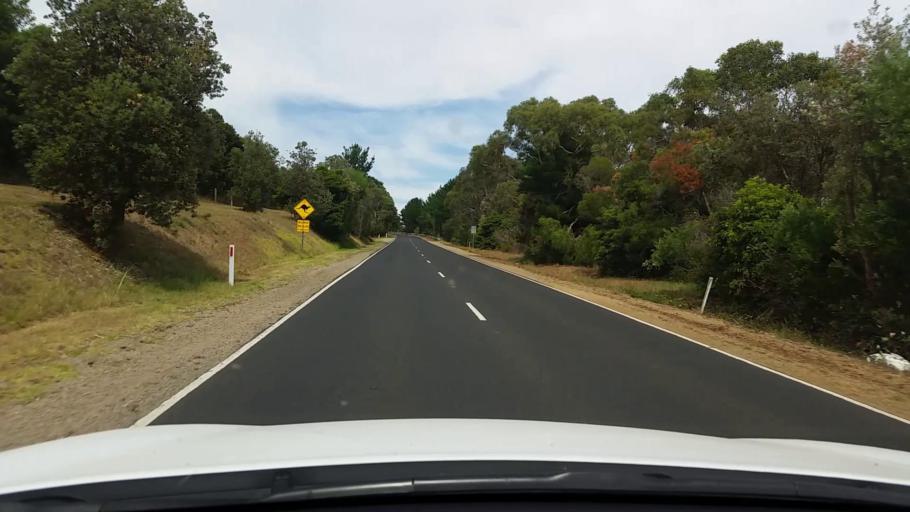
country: AU
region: Victoria
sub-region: Mornington Peninsula
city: Merricks
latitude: -38.4358
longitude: 145.0405
